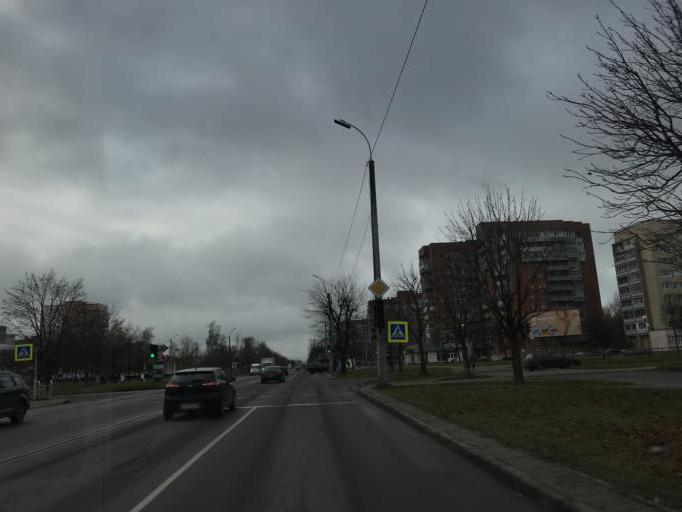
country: BY
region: Mogilev
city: Mahilyow
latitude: 53.8750
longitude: 30.3324
